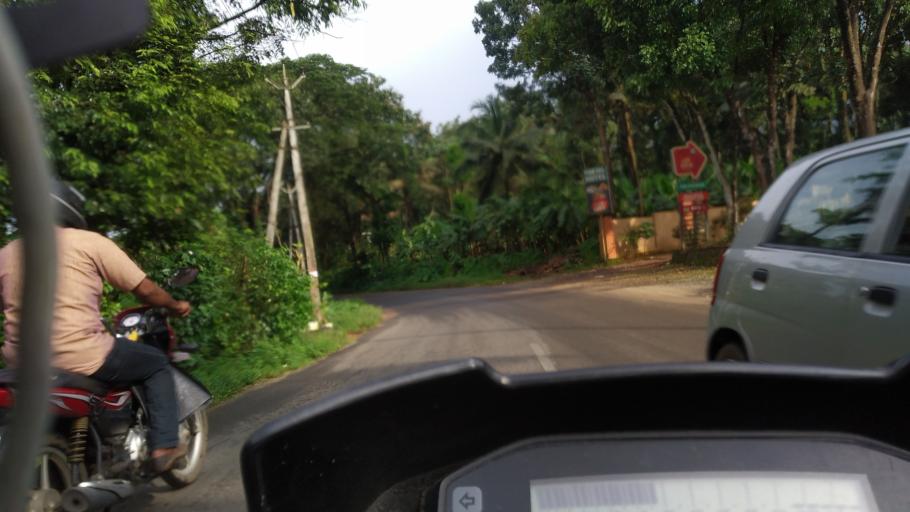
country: IN
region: Kerala
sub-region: Ernakulam
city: Kotamangalam
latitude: 10.0520
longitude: 76.7079
